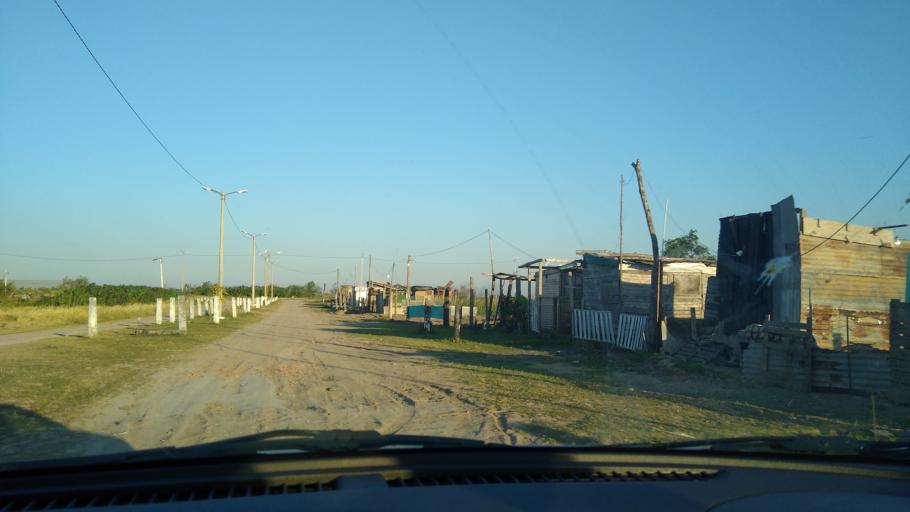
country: AR
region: Chaco
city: Puerto Vilelas
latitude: -27.5076
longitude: -58.9517
